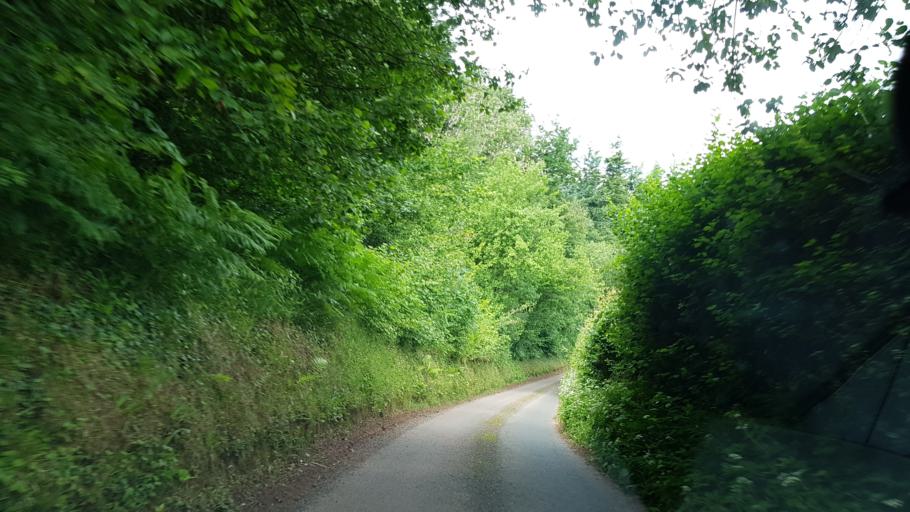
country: GB
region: Wales
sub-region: Monmouthshire
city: Llanarth
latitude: 51.8007
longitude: -2.8335
